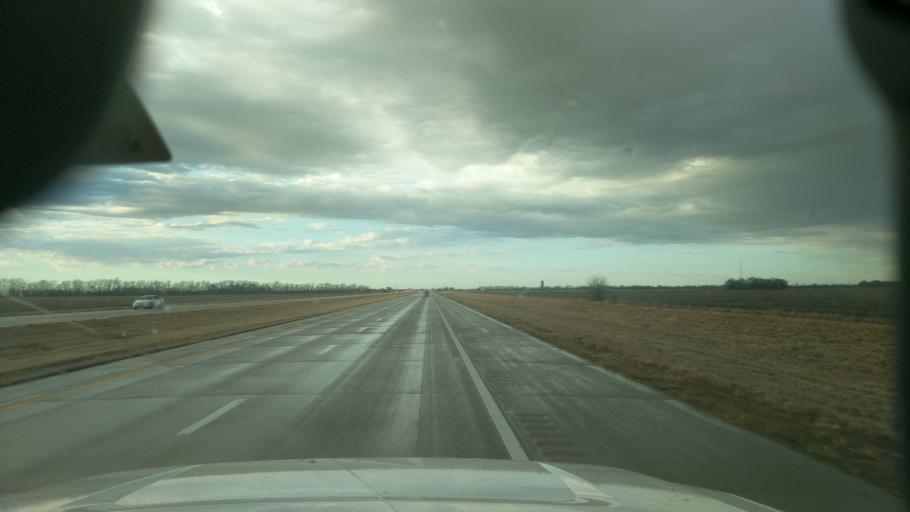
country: US
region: Kansas
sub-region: Harvey County
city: North Newton
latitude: 38.0926
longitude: -97.3607
